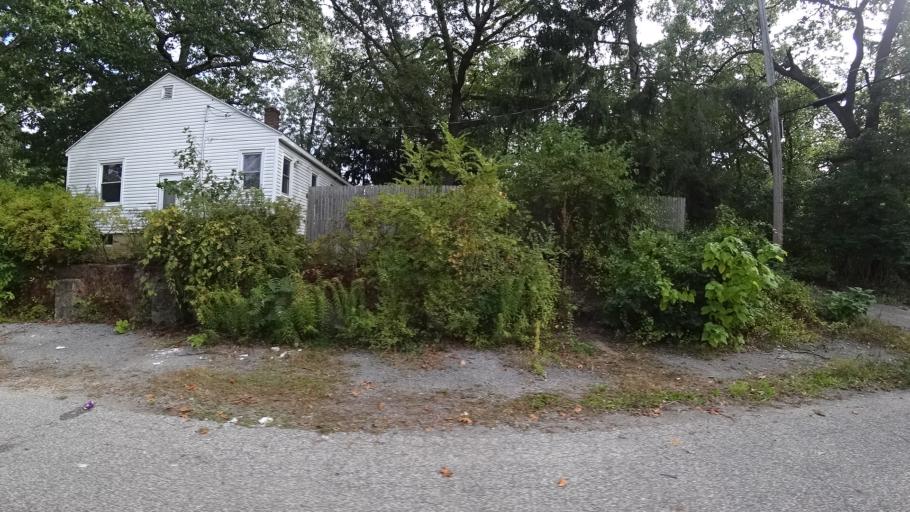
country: US
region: Indiana
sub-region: LaPorte County
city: Michigan City
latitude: 41.7141
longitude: -86.8803
